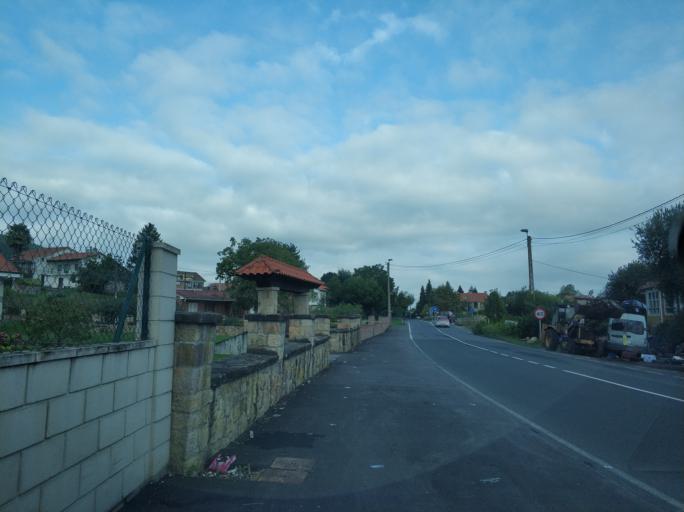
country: ES
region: Cantabria
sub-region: Provincia de Cantabria
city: Puente Viesgo
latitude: 43.3142
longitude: -3.9492
